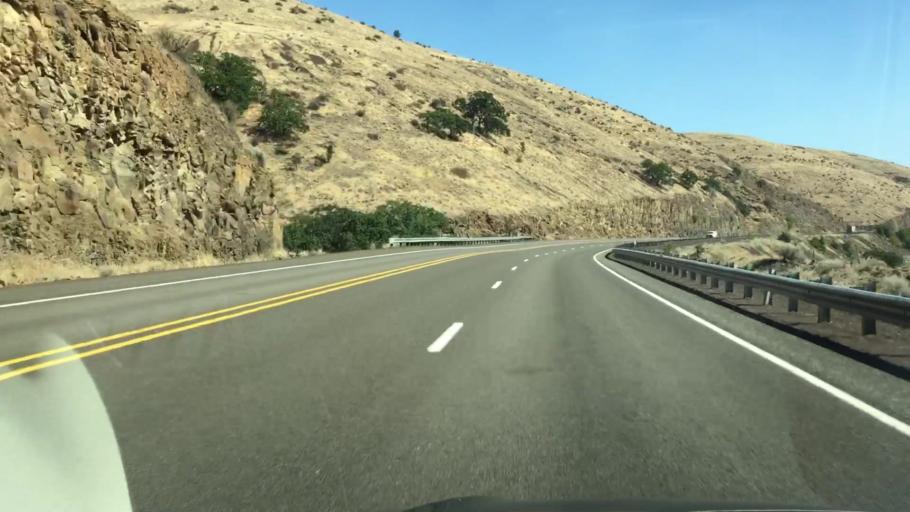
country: US
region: Oregon
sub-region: Wasco County
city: The Dalles
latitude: 45.2919
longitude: -121.1782
